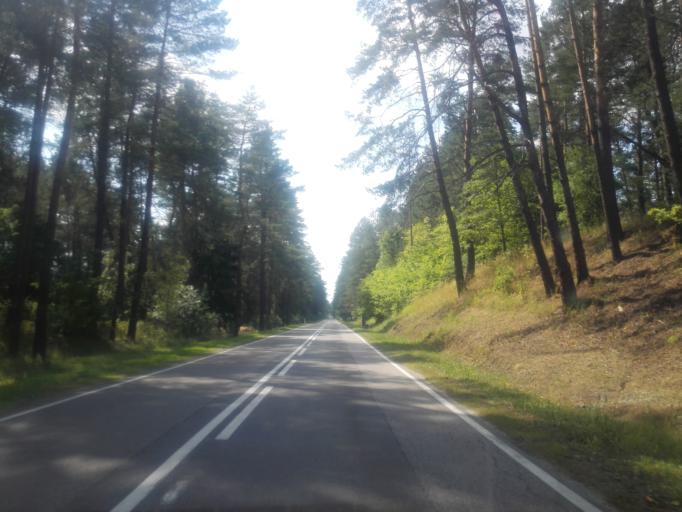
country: PL
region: Podlasie
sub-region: Powiat augustowski
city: Augustow
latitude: 53.8470
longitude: 23.0408
